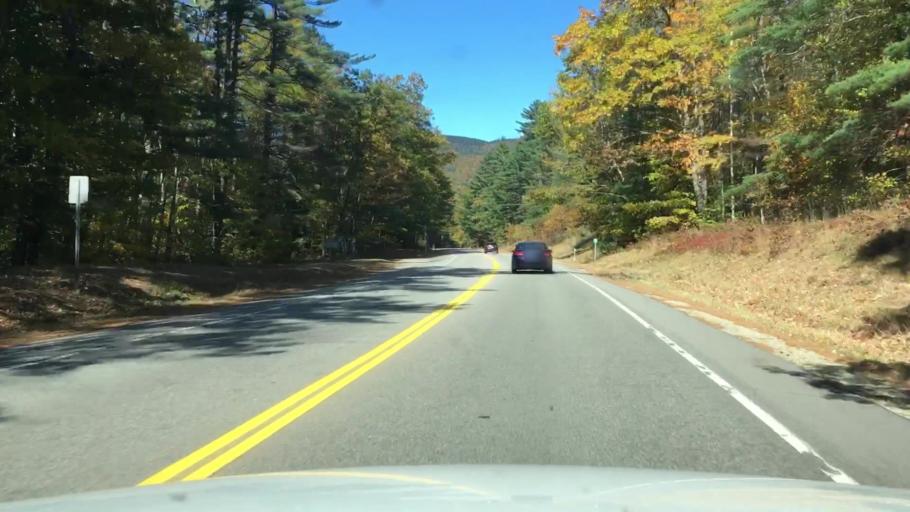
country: US
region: New Hampshire
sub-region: Carroll County
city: Tamworth
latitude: 43.9085
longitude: -71.2338
